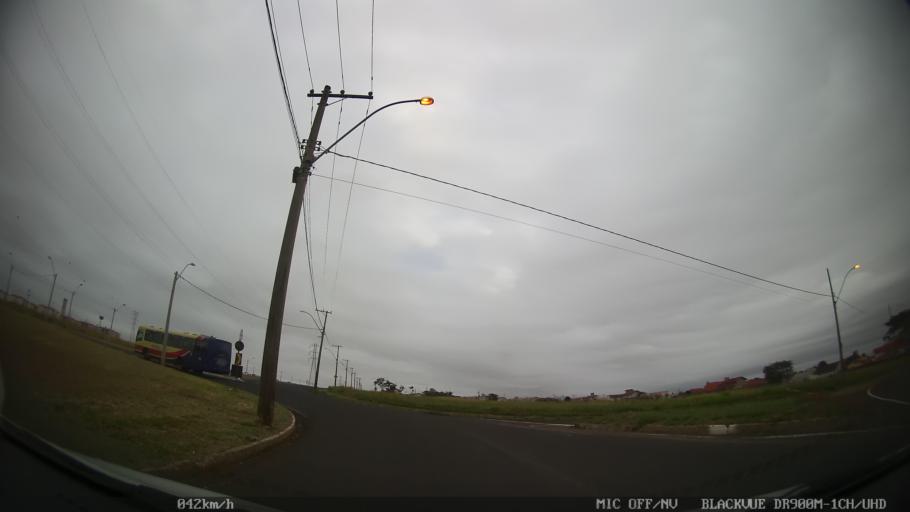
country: BR
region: Sao Paulo
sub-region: Sao Jose Do Rio Preto
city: Sao Jose do Rio Preto
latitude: -20.8413
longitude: -49.4148
